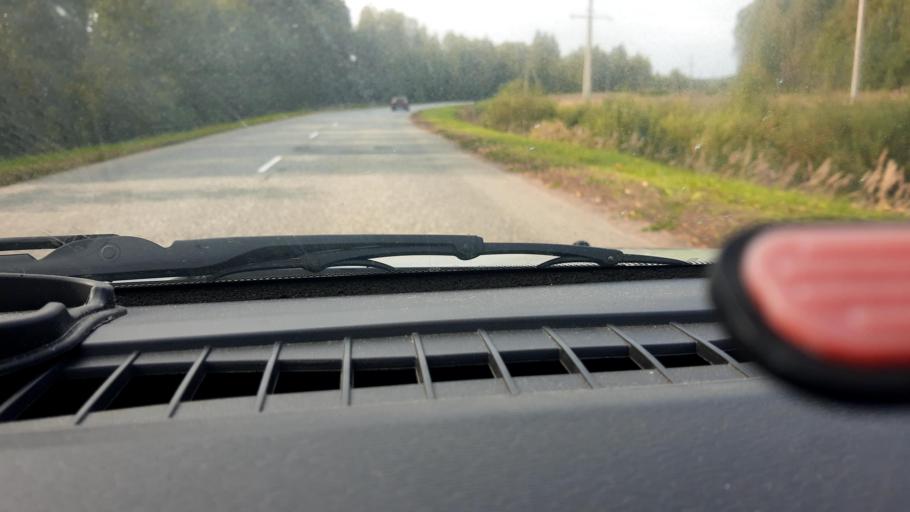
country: RU
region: Nizjnij Novgorod
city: Prudy
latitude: 57.3624
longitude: 46.1857
